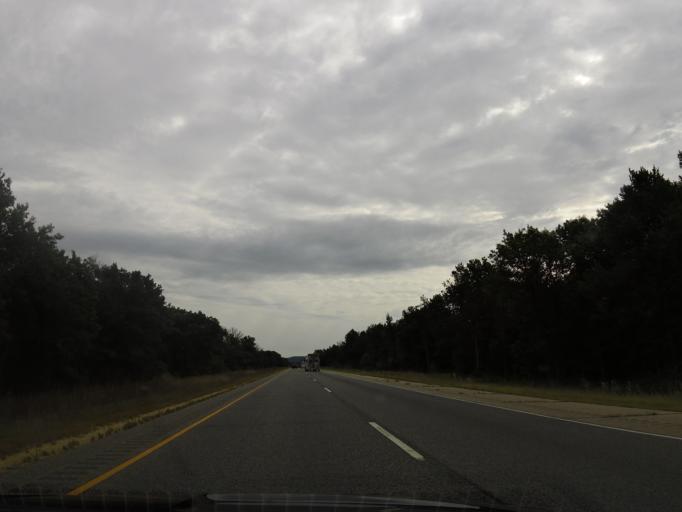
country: US
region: Wisconsin
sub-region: Monroe County
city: Sparta
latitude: 43.9430
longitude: -90.7017
